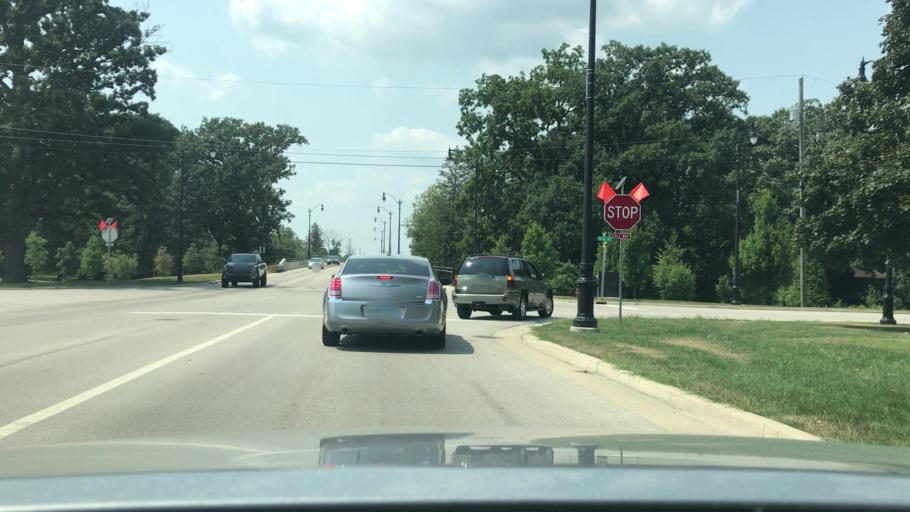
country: US
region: Illinois
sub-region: Will County
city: Plainfield
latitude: 41.5938
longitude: -88.2205
